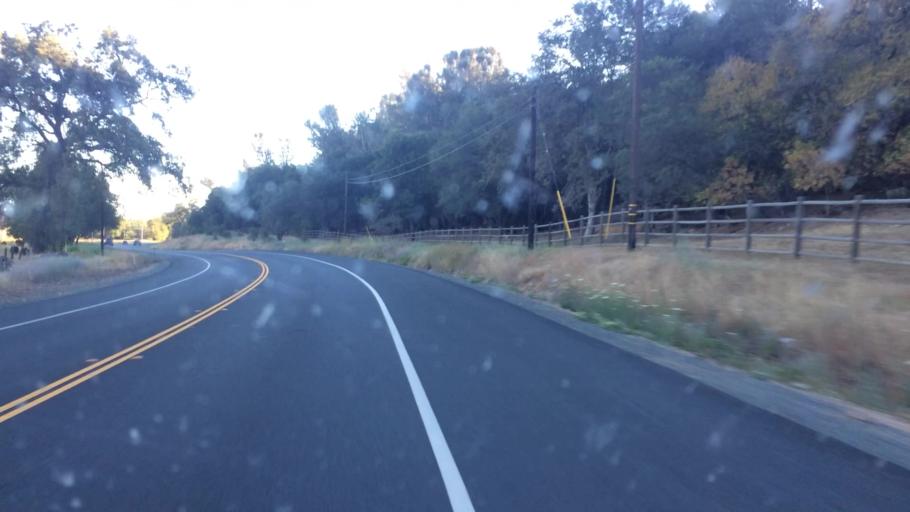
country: US
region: California
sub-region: El Dorado County
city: Deer Park
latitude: 38.6586
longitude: -120.8535
